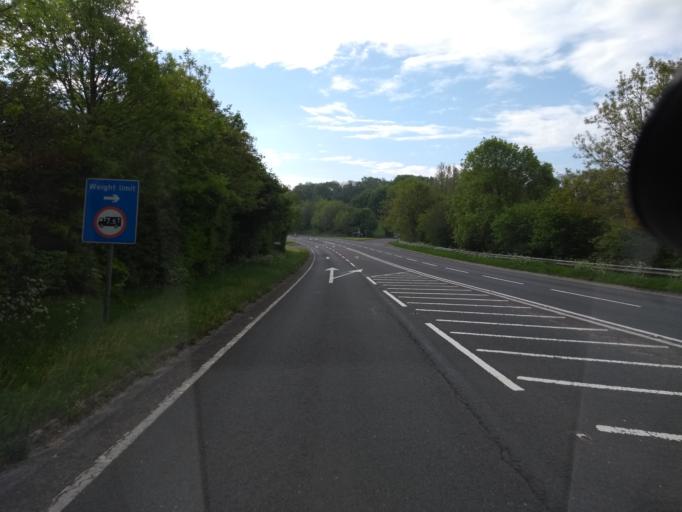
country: GB
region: England
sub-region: Dorset
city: Lyme Regis
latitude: 50.7536
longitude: -2.9343
